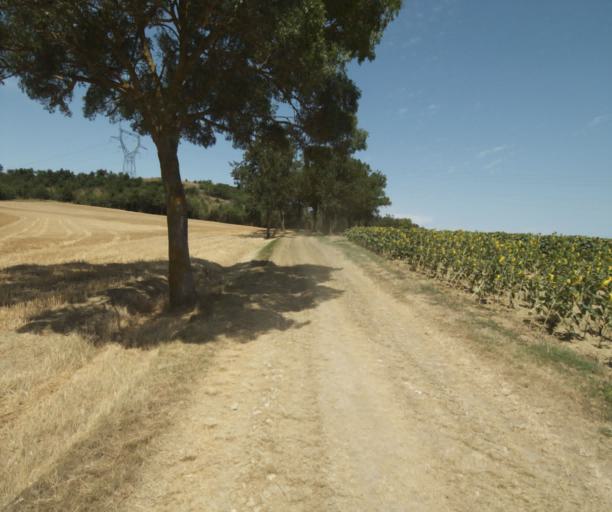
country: FR
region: Midi-Pyrenees
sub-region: Departement de la Haute-Garonne
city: Saint-Felix-Lauragais
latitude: 43.4250
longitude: 1.8833
